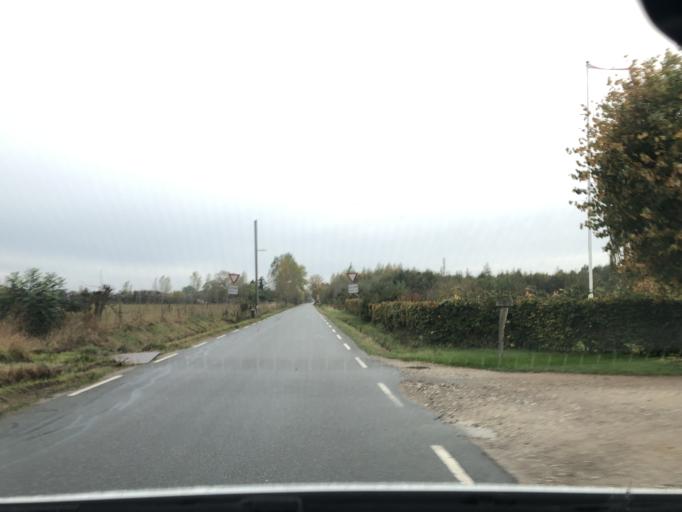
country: DK
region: Capital Region
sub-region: Tarnby Kommune
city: Tarnby
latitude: 55.5689
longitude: 12.5876
